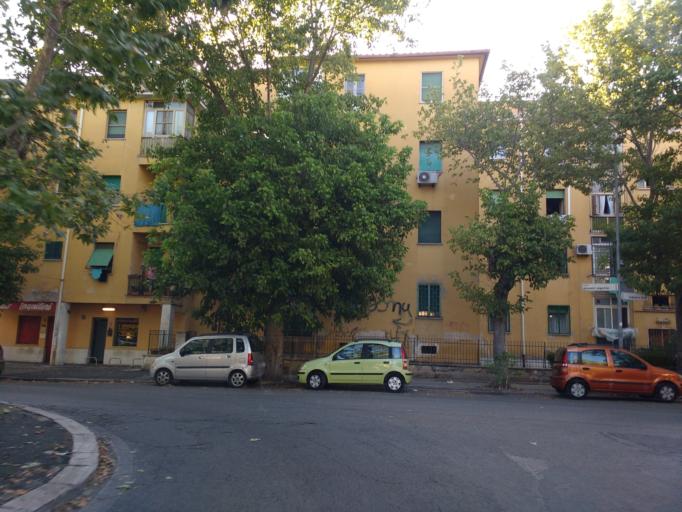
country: IT
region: Latium
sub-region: Citta metropolitana di Roma Capitale
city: Acilia-Castel Fusano-Ostia Antica
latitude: 41.7780
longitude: 12.3553
